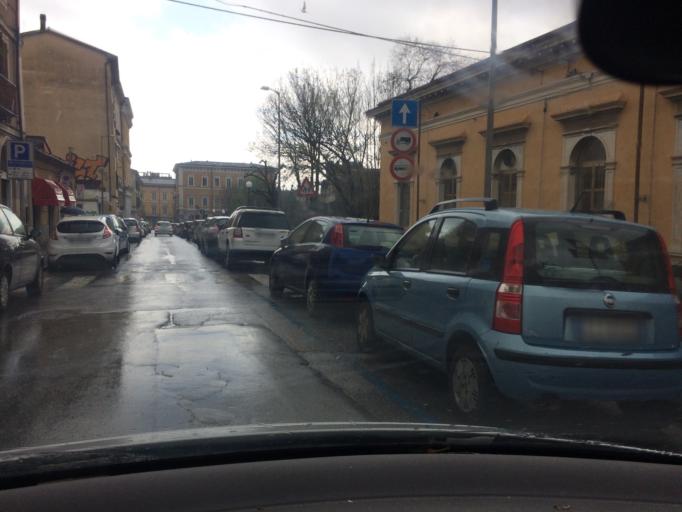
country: IT
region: Tuscany
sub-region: Provincia di Massa-Carrara
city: Carrara
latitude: 44.0793
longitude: 10.1017
